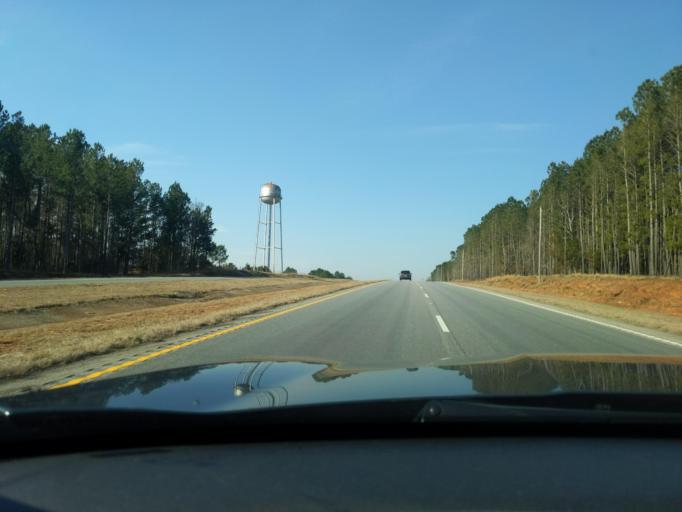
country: US
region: South Carolina
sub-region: Abbeville County
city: Calhoun Falls
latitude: 34.1087
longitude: -82.5206
